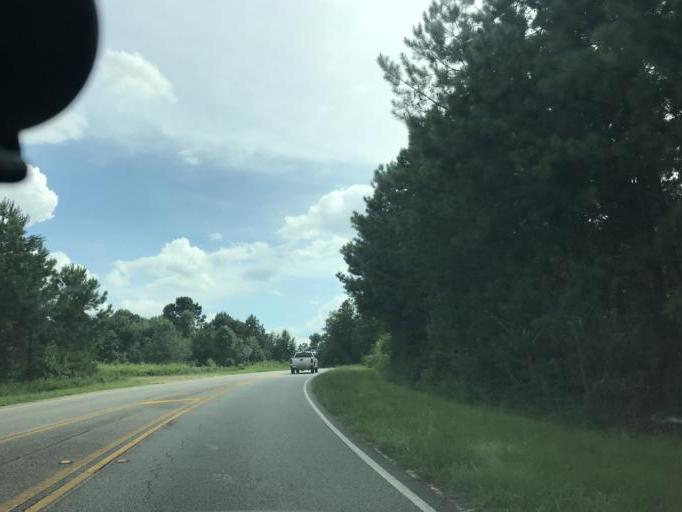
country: US
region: Georgia
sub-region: Forsyth County
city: Cumming
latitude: 34.2978
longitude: -84.1537
